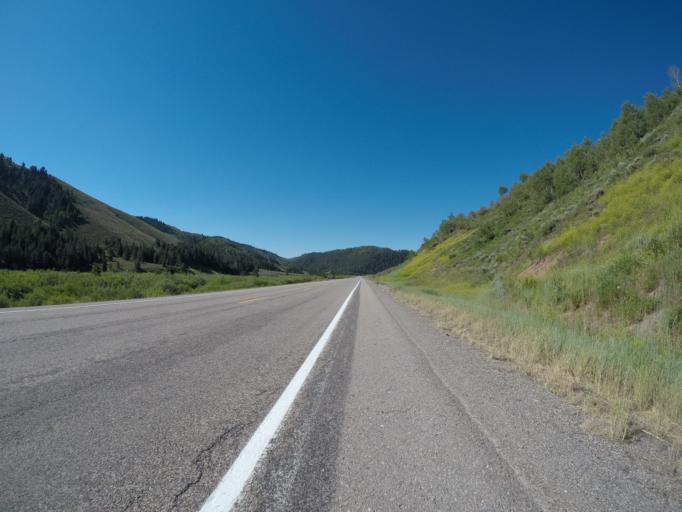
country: US
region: Wyoming
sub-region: Lincoln County
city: Afton
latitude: 42.4777
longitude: -110.9644
